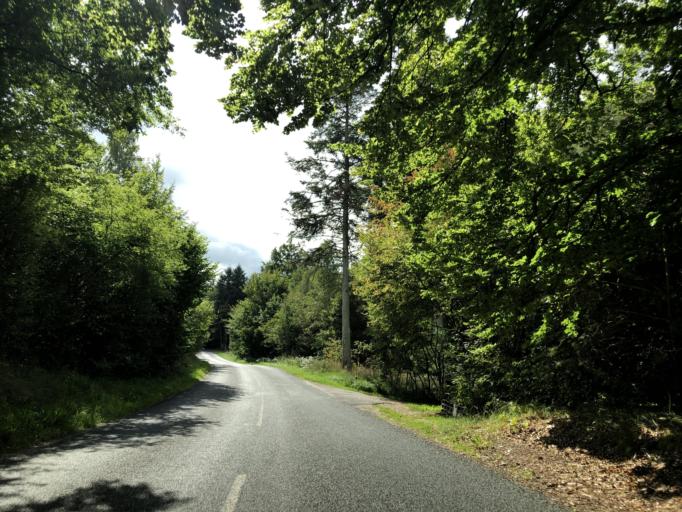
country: DK
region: North Denmark
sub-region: Vesthimmerland Kommune
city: Alestrup
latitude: 56.6092
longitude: 9.4343
